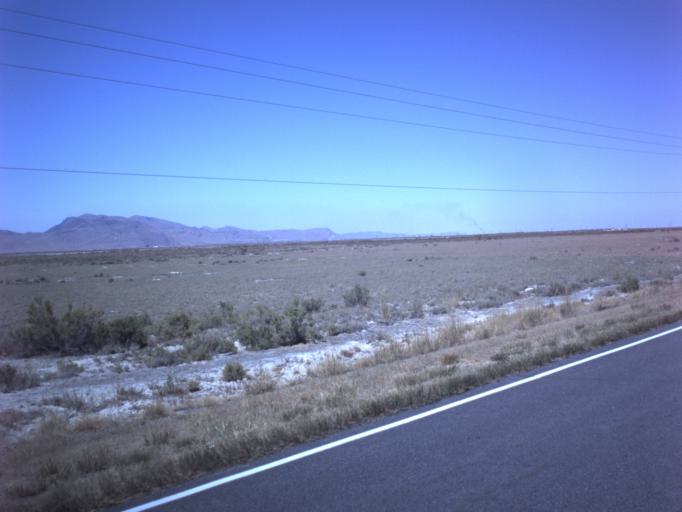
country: US
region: Utah
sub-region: Tooele County
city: Grantsville
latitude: 40.7250
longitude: -112.6590
